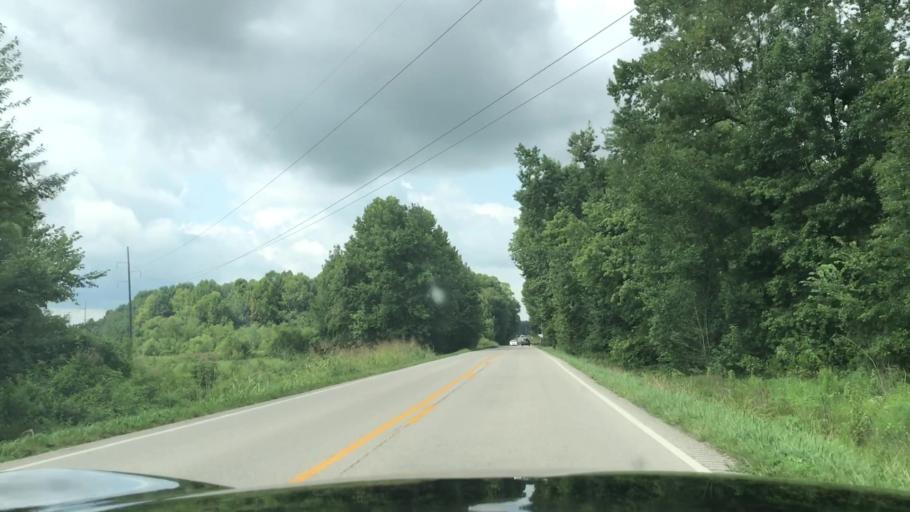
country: US
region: Kentucky
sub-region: Butler County
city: Morgantown
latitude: 37.1967
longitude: -86.7437
